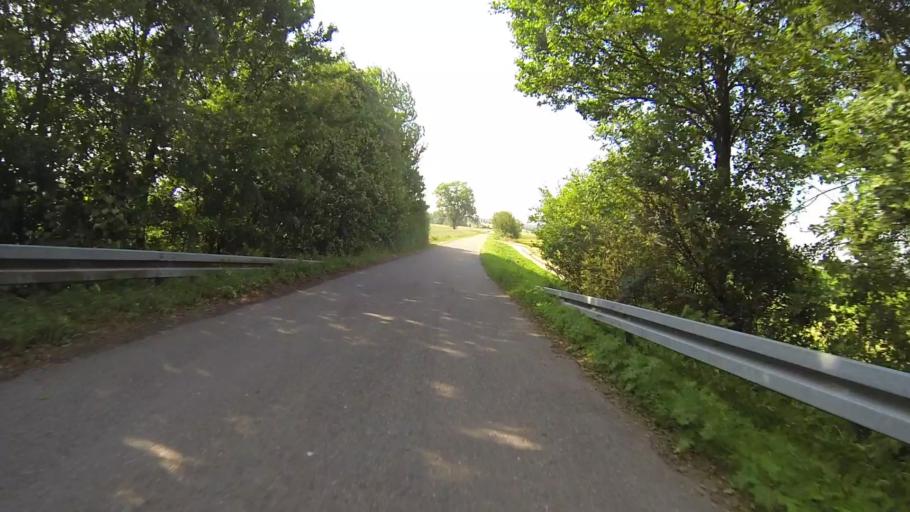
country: DE
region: Bavaria
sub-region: Swabia
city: Neu-Ulm
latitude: 48.3927
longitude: 10.0517
